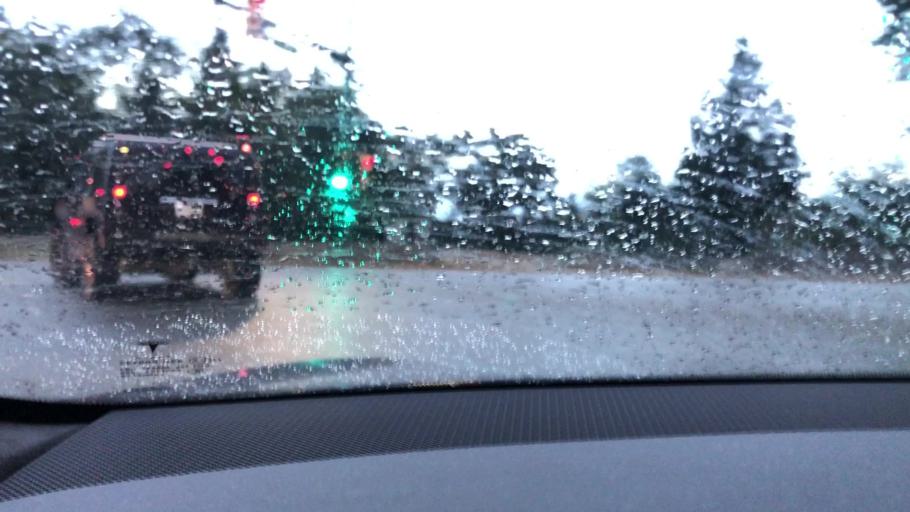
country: CA
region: British Columbia
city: Burnaby
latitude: 49.2039
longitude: -122.9996
